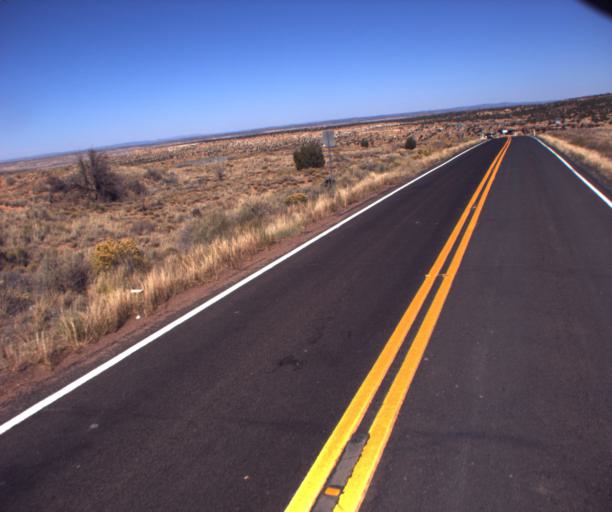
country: US
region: Arizona
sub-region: Navajo County
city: First Mesa
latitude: 35.9256
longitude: -110.6616
